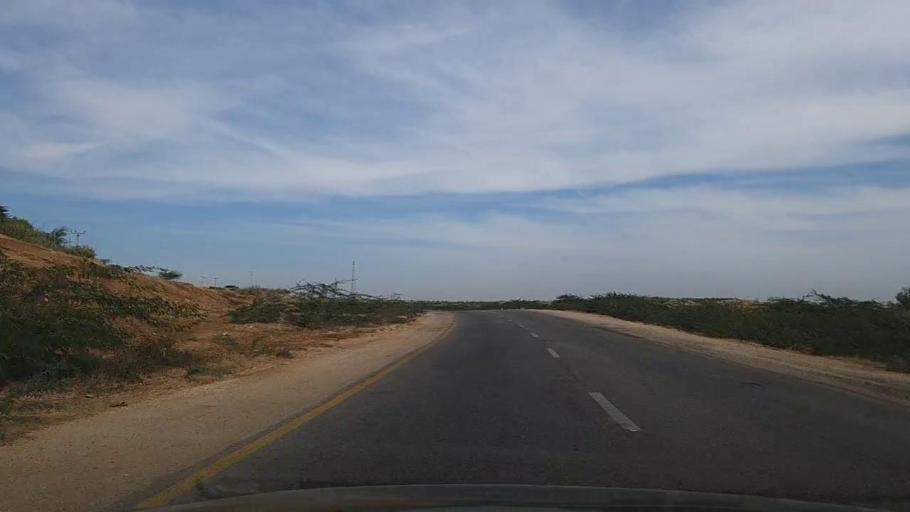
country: PK
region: Sindh
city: Thatta
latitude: 24.8570
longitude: 68.0219
